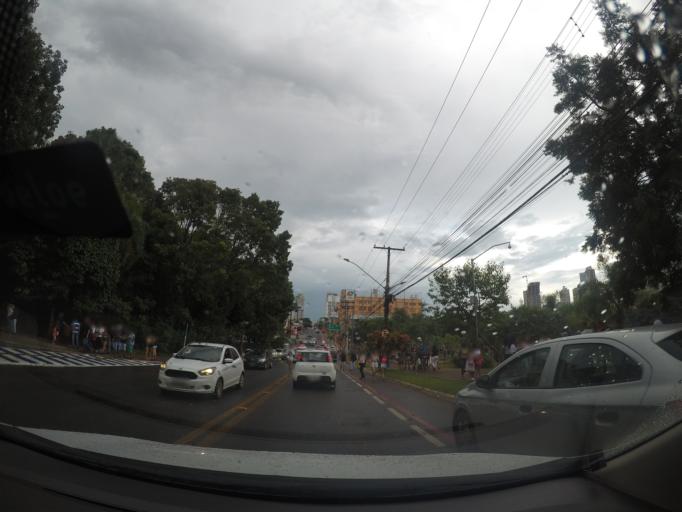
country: BR
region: Goias
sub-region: Goiania
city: Goiania
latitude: -16.7083
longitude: -49.2720
